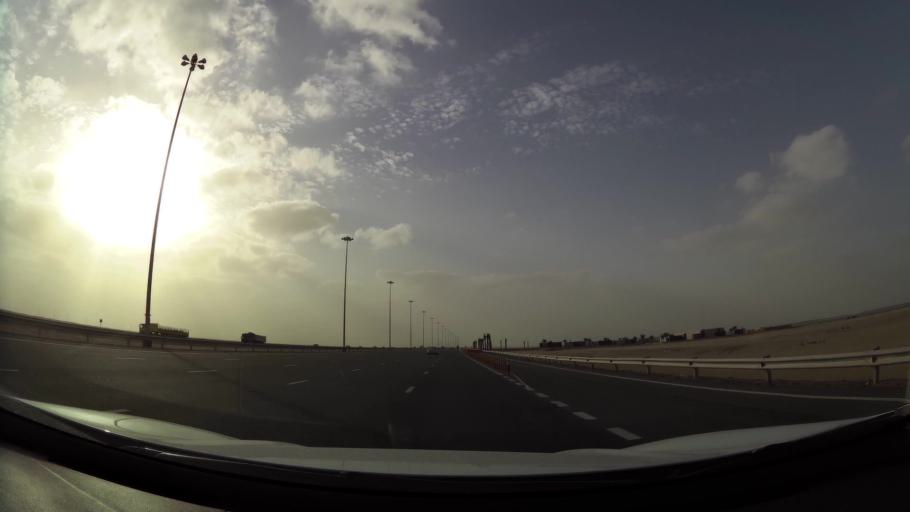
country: AE
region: Abu Dhabi
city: Abu Dhabi
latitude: 24.5088
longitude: 54.5559
